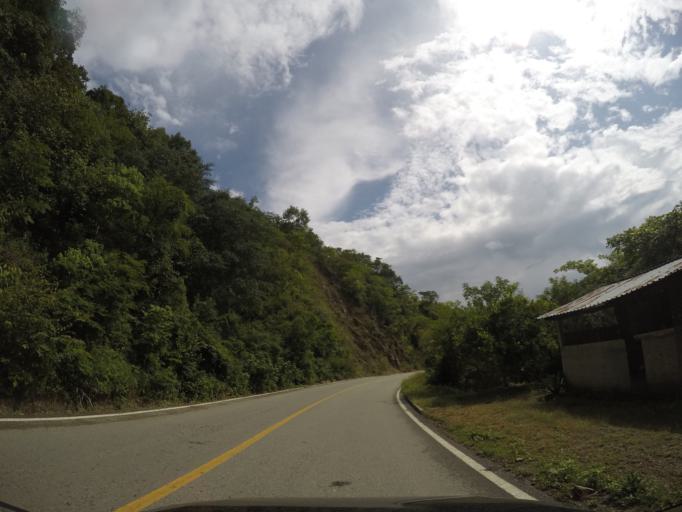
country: MX
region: Oaxaca
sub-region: San Jeronimo Coatlan
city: San Cristobal Honduras
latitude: 16.3781
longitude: -97.0768
